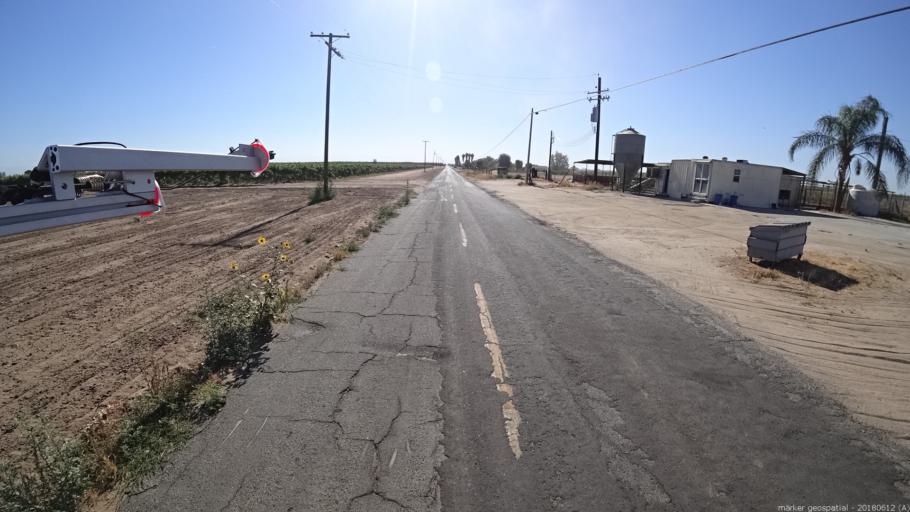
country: US
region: California
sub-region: Madera County
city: Fairmead
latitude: 37.0110
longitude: -120.1755
